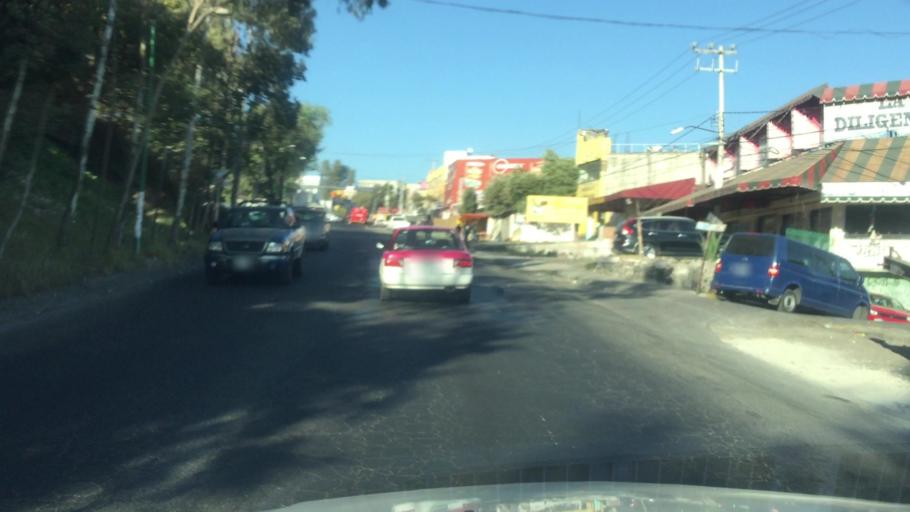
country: MX
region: Mexico City
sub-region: Tlalpan
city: Lomas de Tepemecatl
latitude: 19.2676
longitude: -99.2095
